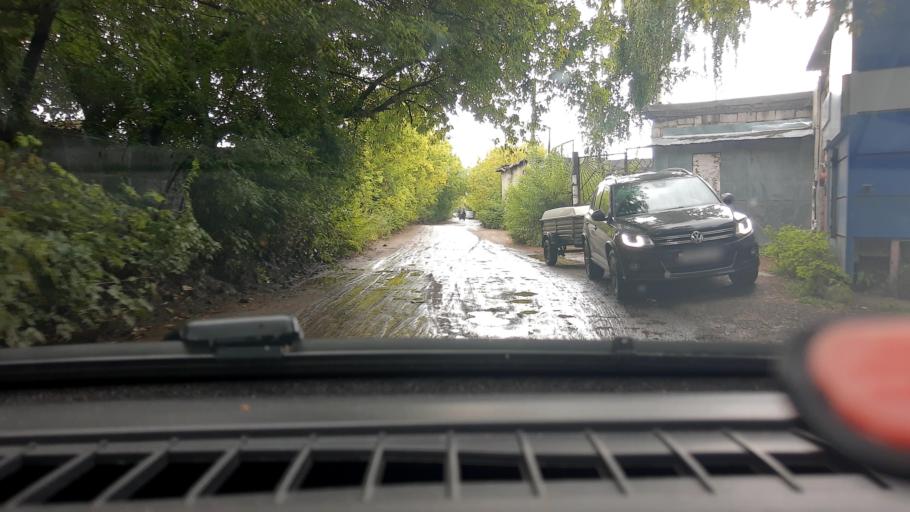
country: RU
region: Nizjnij Novgorod
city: Gorbatovka
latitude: 56.2559
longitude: 43.8313
